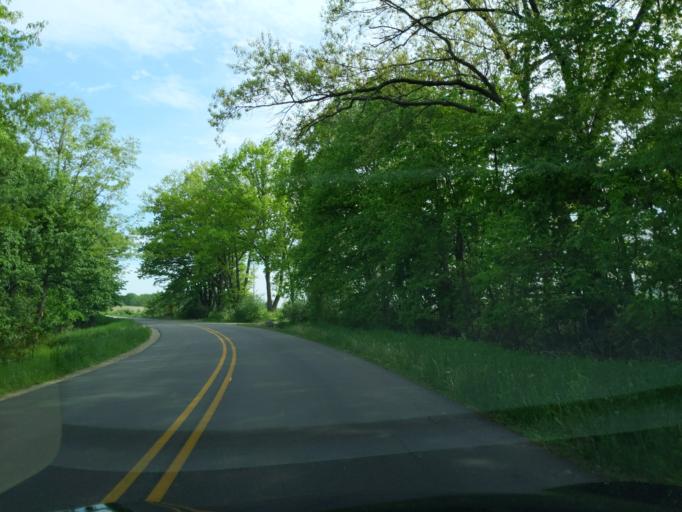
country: US
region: Michigan
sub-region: Ingham County
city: Leslie
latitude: 42.4194
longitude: -84.3568
